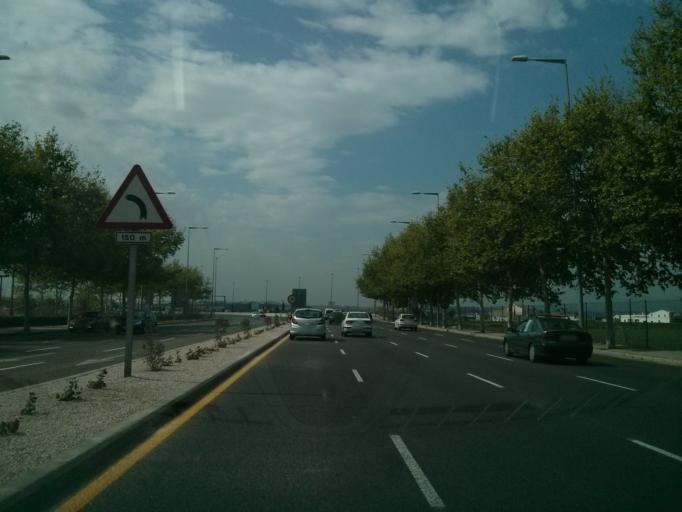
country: ES
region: Valencia
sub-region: Provincia de Valencia
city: Tavernes Blanques
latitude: 39.5013
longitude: -0.3900
